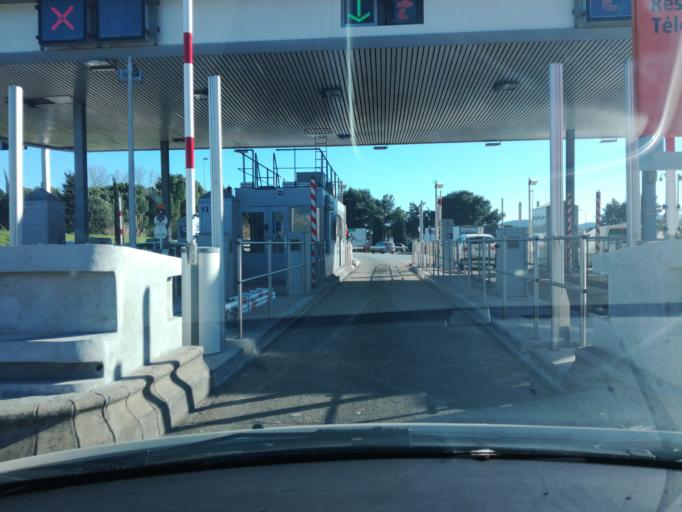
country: FR
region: Provence-Alpes-Cote d'Azur
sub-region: Departement du Var
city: Puget-sur-Argens
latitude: 43.4570
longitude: 6.6894
